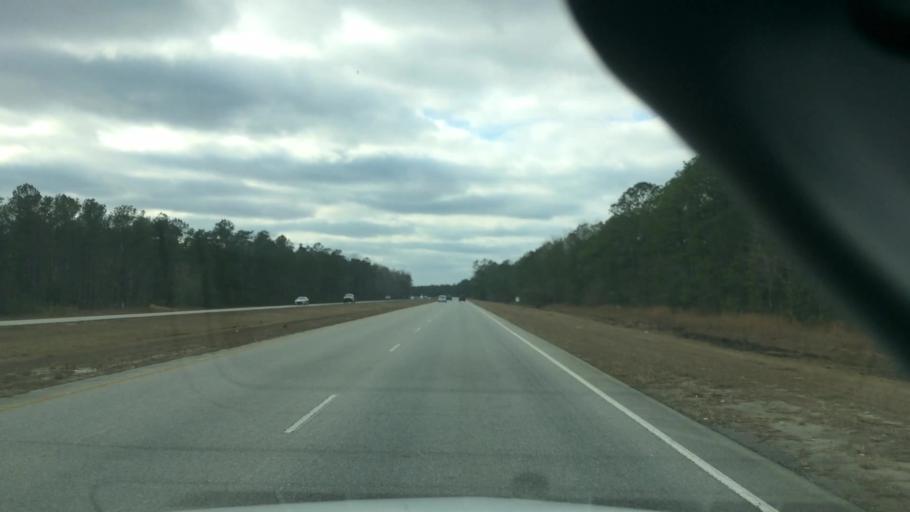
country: US
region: North Carolina
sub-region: Brunswick County
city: Bolivia
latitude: 34.0773
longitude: -78.1484
